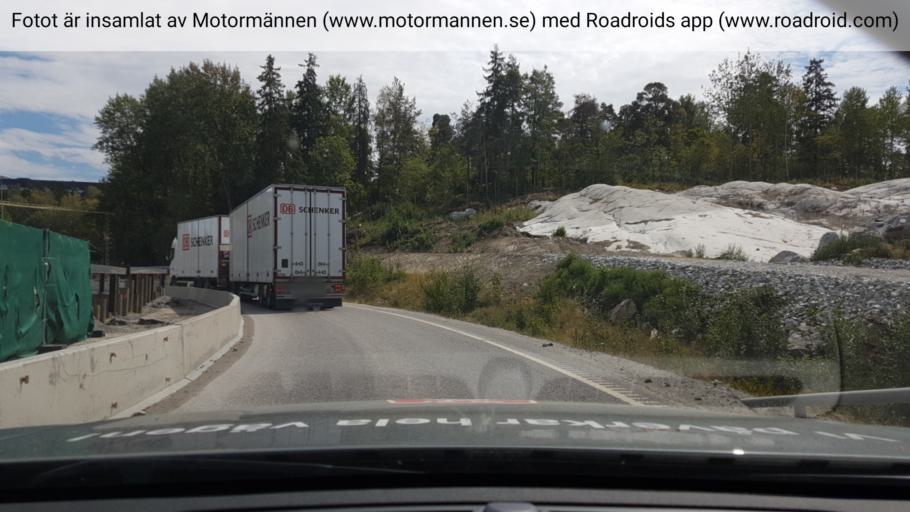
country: SE
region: Stockholm
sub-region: Jarfalla Kommun
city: Jakobsberg
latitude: 59.4000
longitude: 17.8819
